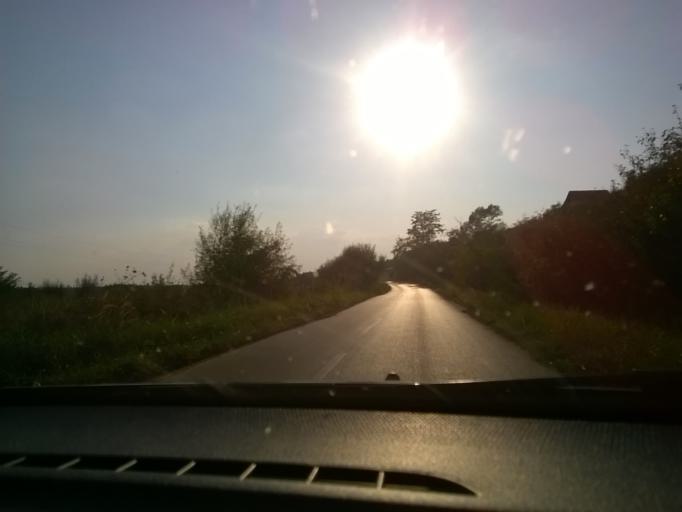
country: RS
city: Kustilj
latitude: 45.1006
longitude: 21.3795
